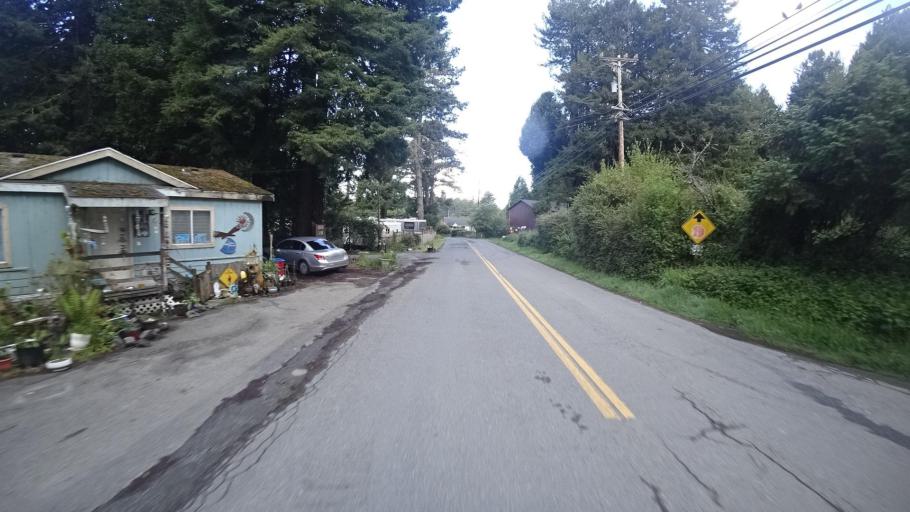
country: US
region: California
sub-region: Humboldt County
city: Westhaven-Moonstone
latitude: 41.0623
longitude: -124.1371
